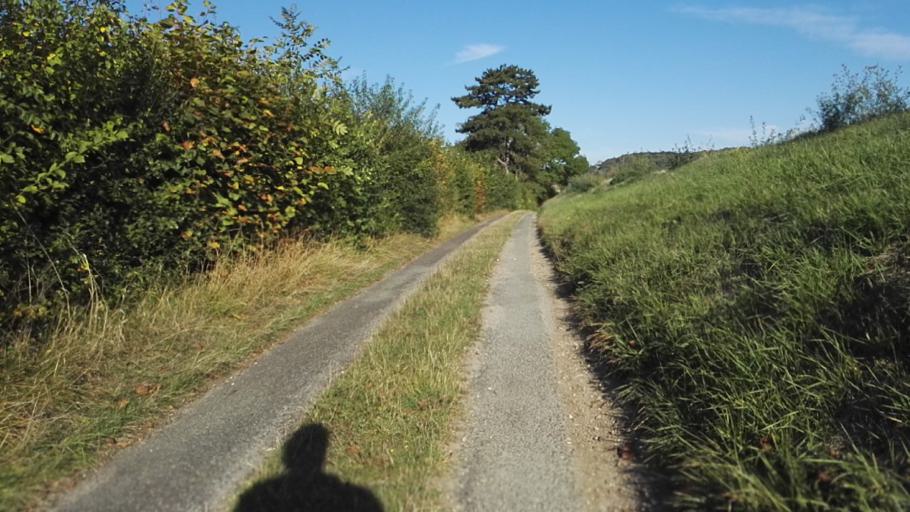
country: FR
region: Haute-Normandie
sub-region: Departement de l'Eure
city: Houlbec-Cocherel
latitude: 49.0534
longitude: 1.3390
